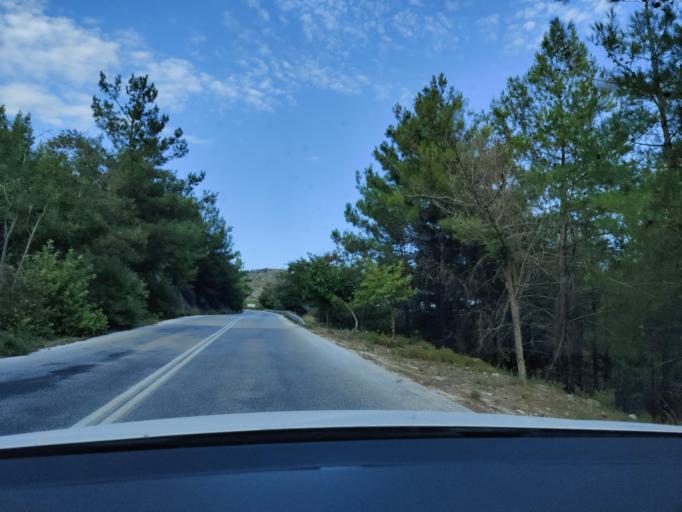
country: GR
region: East Macedonia and Thrace
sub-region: Nomos Kavalas
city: Limenaria
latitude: 40.6186
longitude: 24.6535
